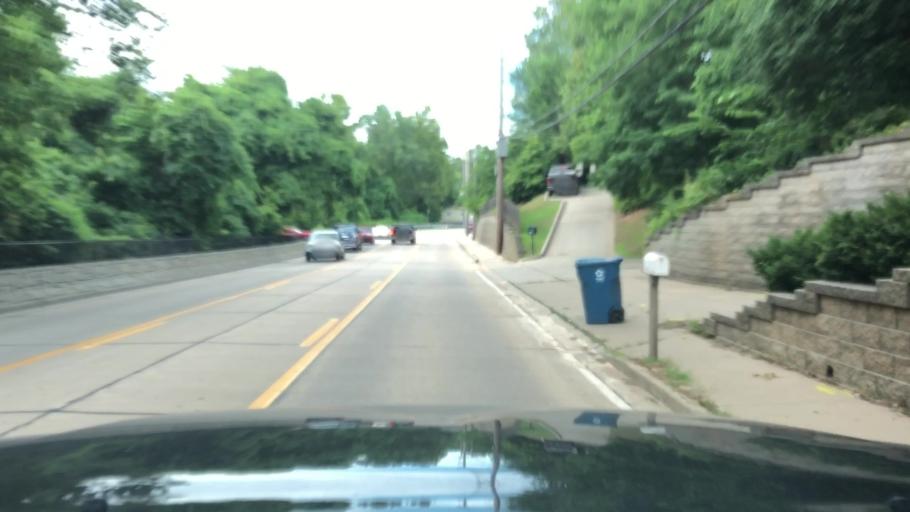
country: US
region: Missouri
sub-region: Saint Charles County
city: Saint Charles
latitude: 38.8117
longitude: -90.5128
